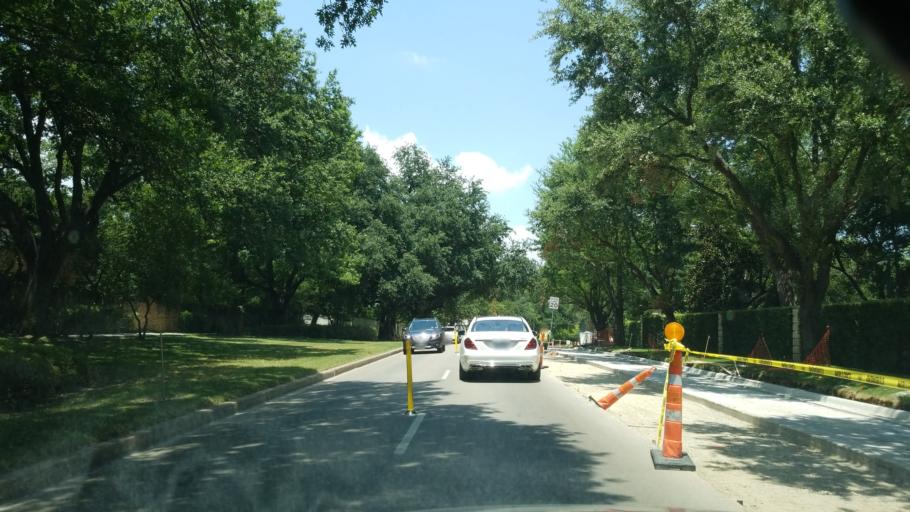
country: US
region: Texas
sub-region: Dallas County
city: Highland Park
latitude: 32.8288
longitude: -96.8043
